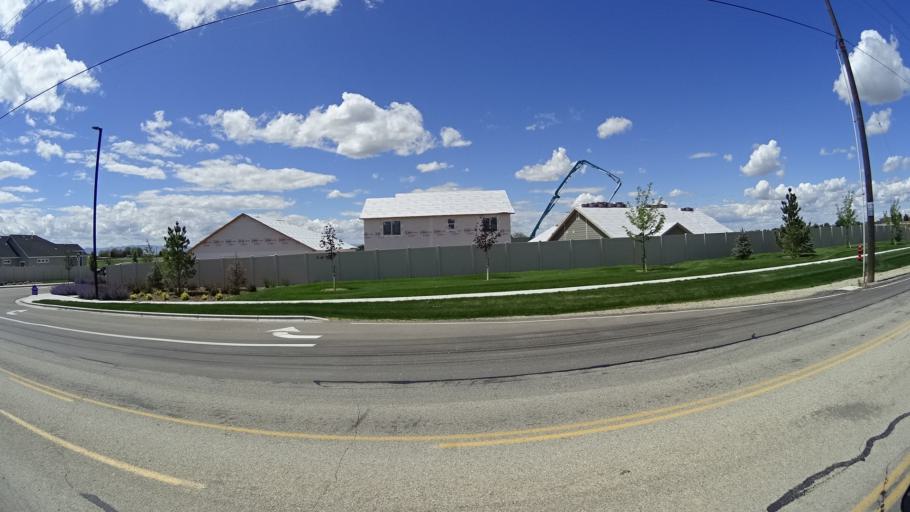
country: US
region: Idaho
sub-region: Ada County
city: Kuna
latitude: 43.5514
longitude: -116.4337
